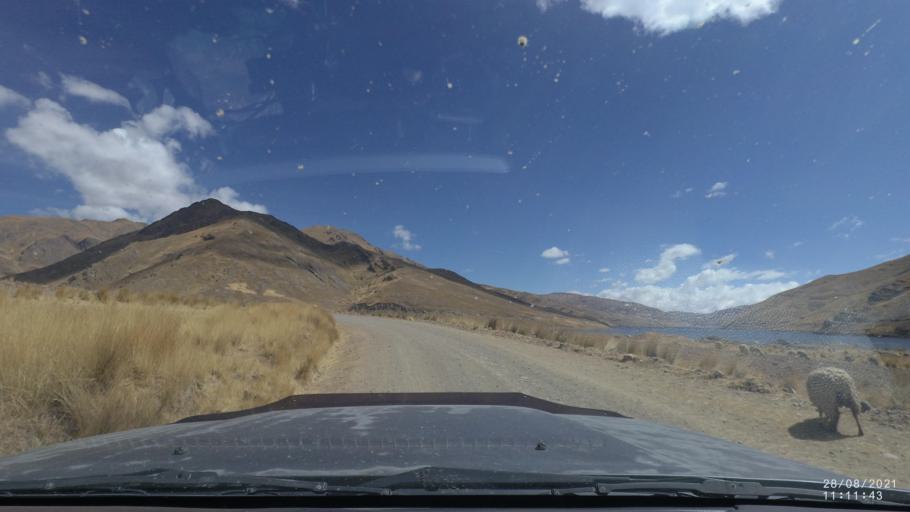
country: BO
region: Cochabamba
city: Cochabamba
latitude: -17.1488
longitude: -66.3140
